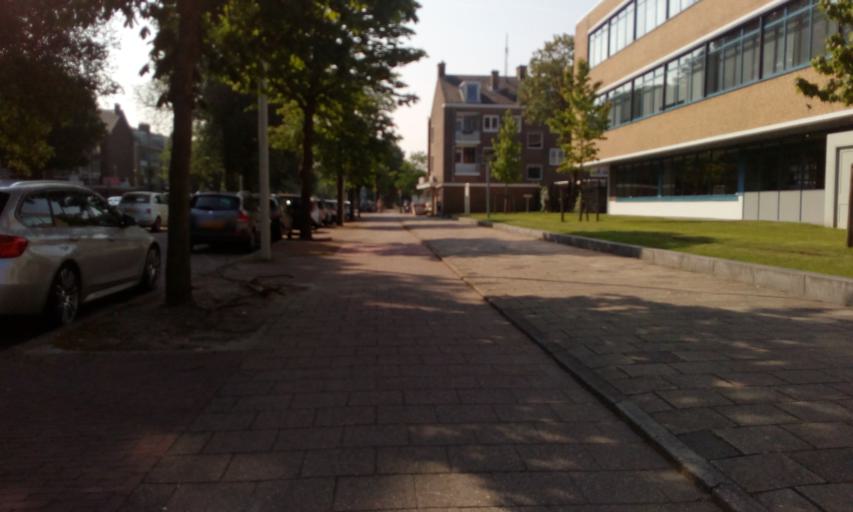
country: NL
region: South Holland
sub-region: Gemeente Leidschendam-Voorburg
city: Voorburg
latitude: 52.0854
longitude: 4.3328
